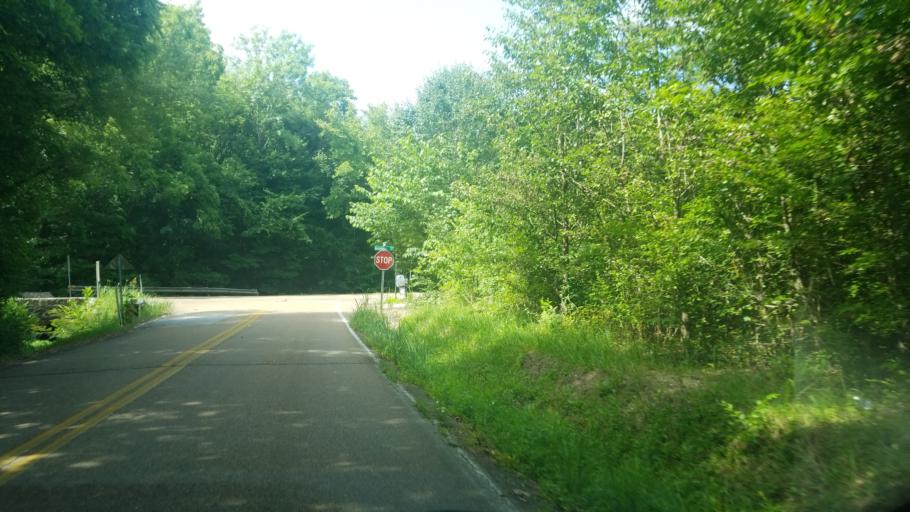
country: US
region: Tennessee
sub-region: Hamilton County
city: Lakesite
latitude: 35.1676
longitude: -85.0658
